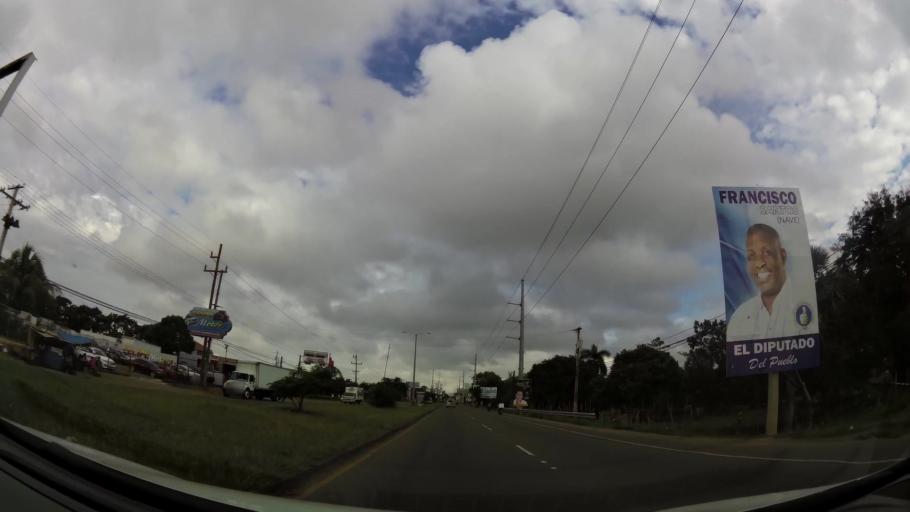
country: DO
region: Santiago
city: Licey al Medio
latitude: 19.4184
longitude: -70.6465
